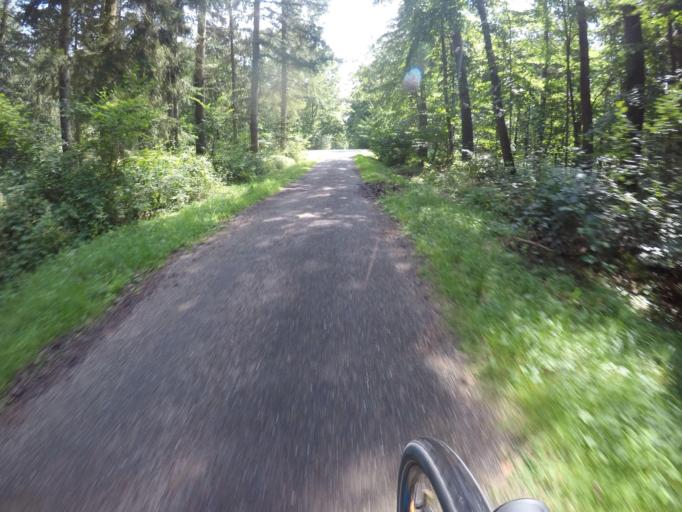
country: DE
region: Baden-Wuerttemberg
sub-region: Karlsruhe Region
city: Hambrucken
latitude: 49.2182
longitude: 8.5704
